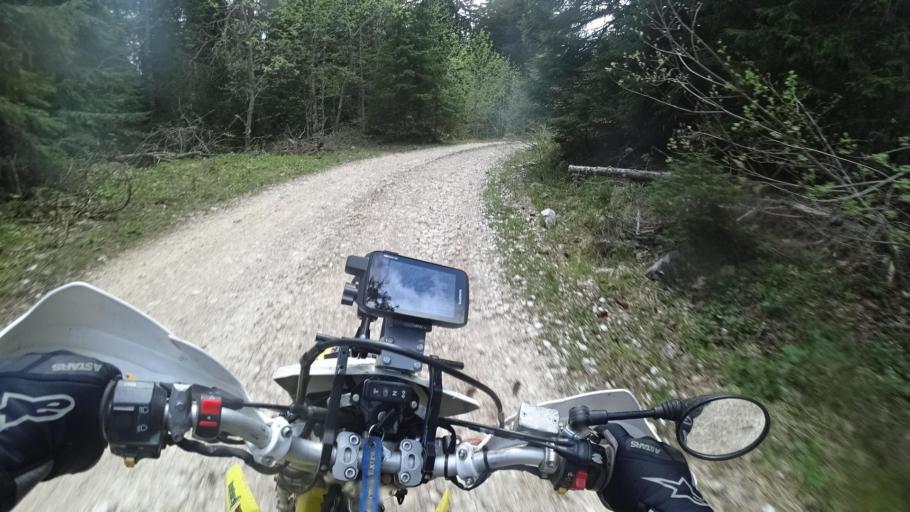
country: BA
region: Republika Srpska
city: Sipovo
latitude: 44.1209
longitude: 17.0783
